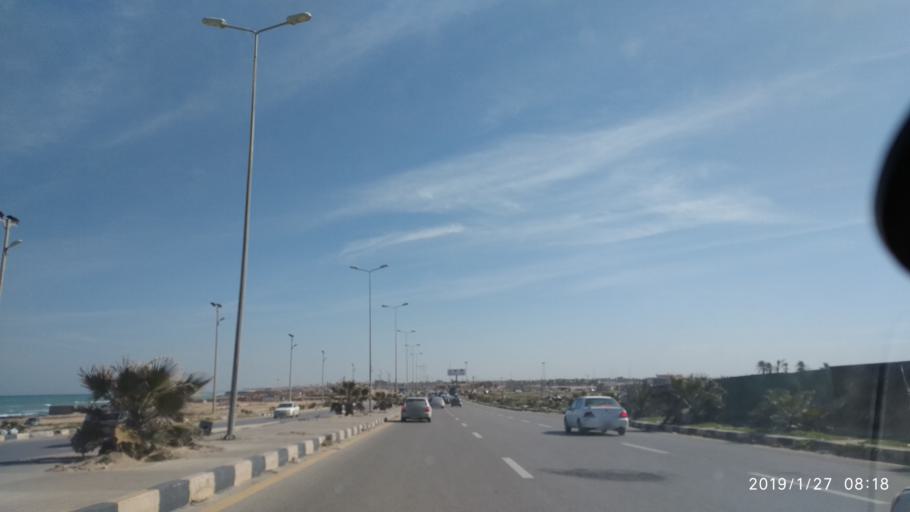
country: LY
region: Tripoli
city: Tagiura
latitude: 32.8974
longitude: 13.3185
